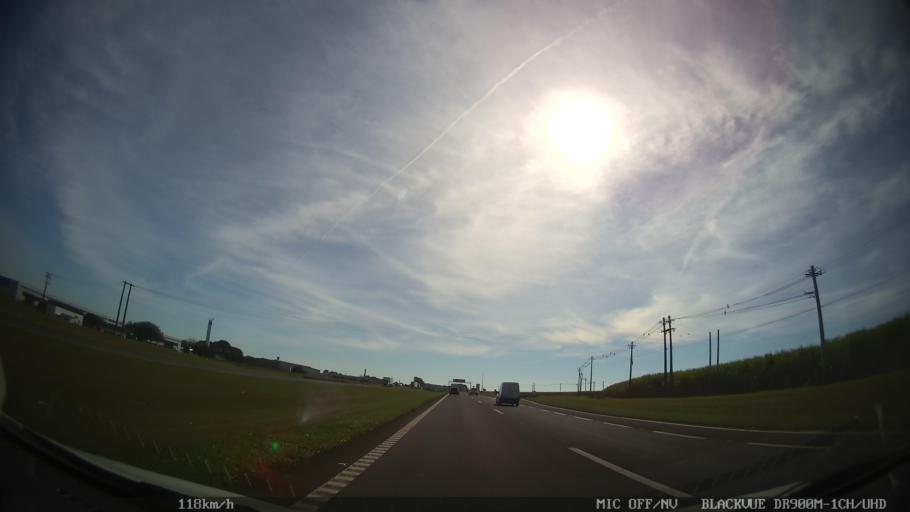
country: BR
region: Sao Paulo
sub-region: Araras
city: Araras
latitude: -22.4191
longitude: -47.3912
